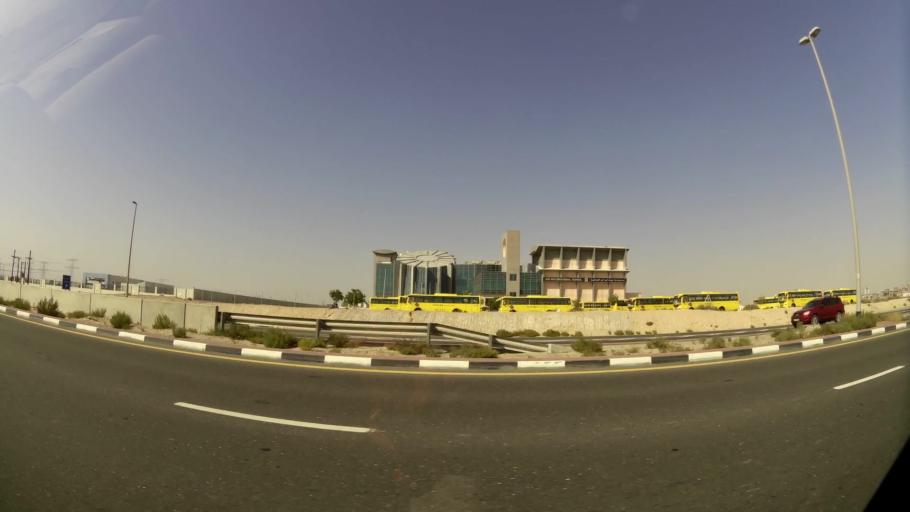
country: AE
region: Dubai
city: Dubai
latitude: 25.0738
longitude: 55.2139
